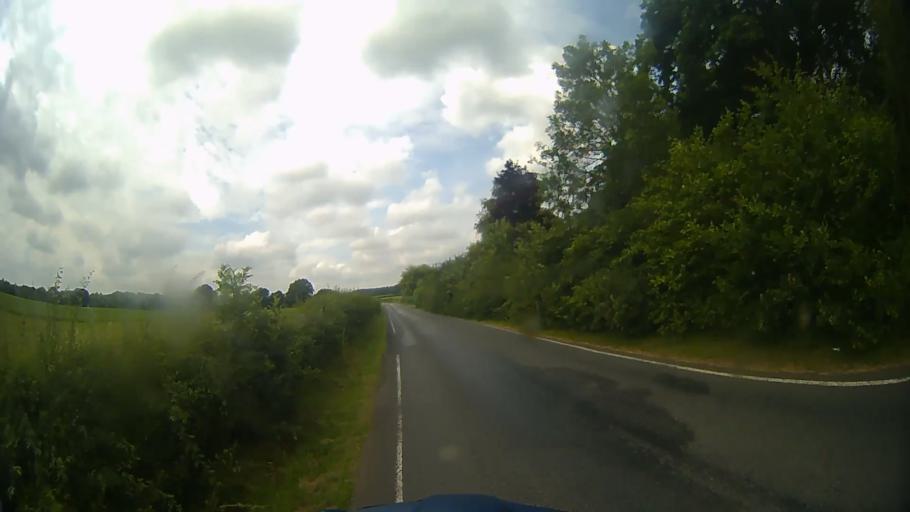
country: GB
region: England
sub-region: Hampshire
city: Kingsley
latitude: 51.1596
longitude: -0.8522
